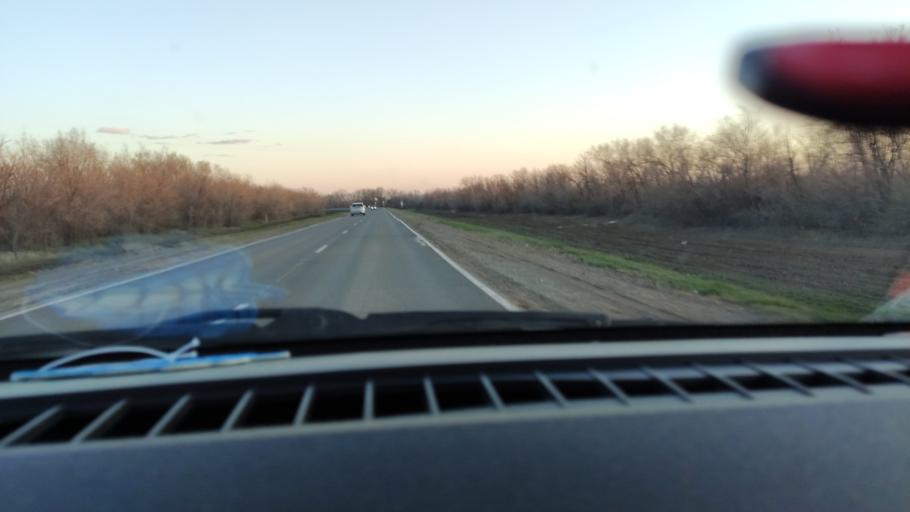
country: RU
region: Saratov
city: Privolzhskiy
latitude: 51.3541
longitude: 46.0438
